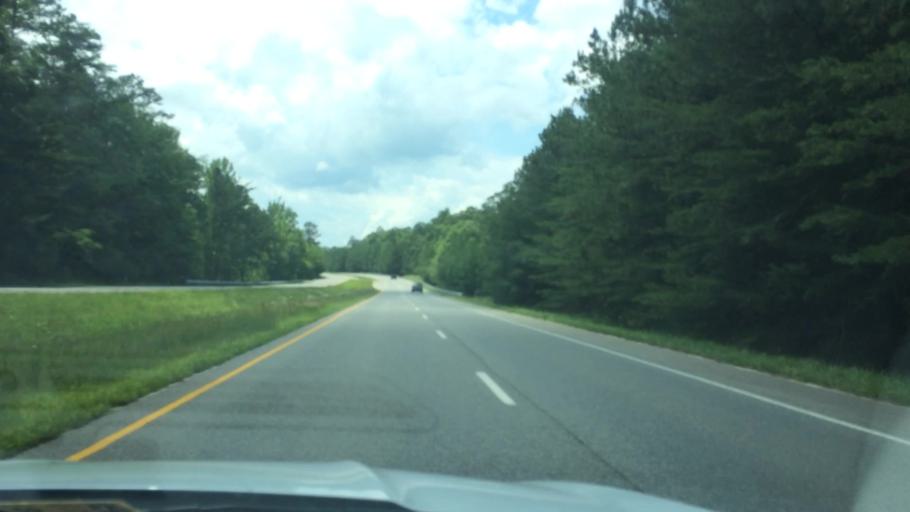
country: US
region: Virginia
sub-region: Middlesex County
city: Saluda
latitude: 37.5648
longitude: -76.6444
